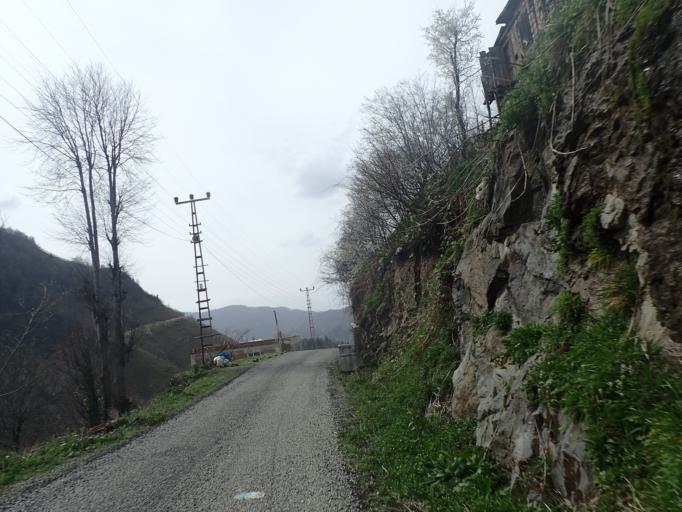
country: TR
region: Ordu
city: Kabaduz
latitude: 40.7764
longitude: 37.9033
